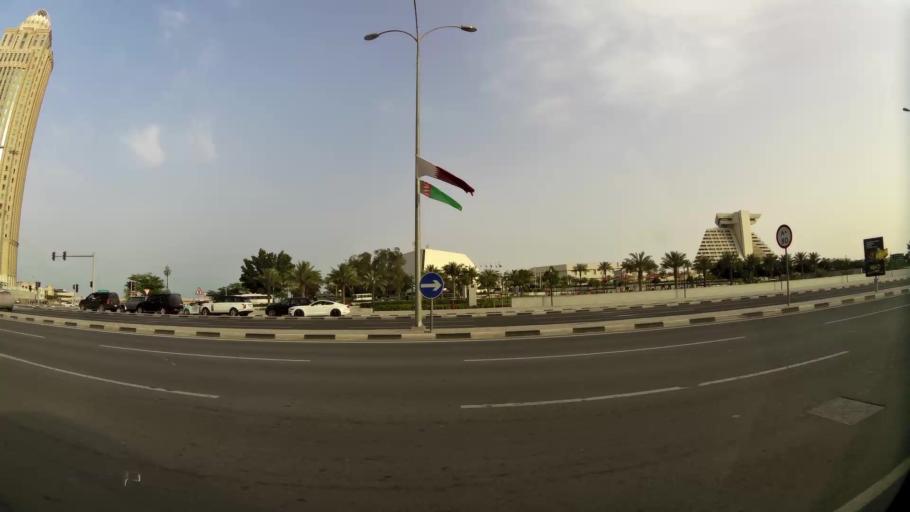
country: QA
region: Baladiyat ad Dawhah
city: Doha
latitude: 25.3223
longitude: 51.5356
